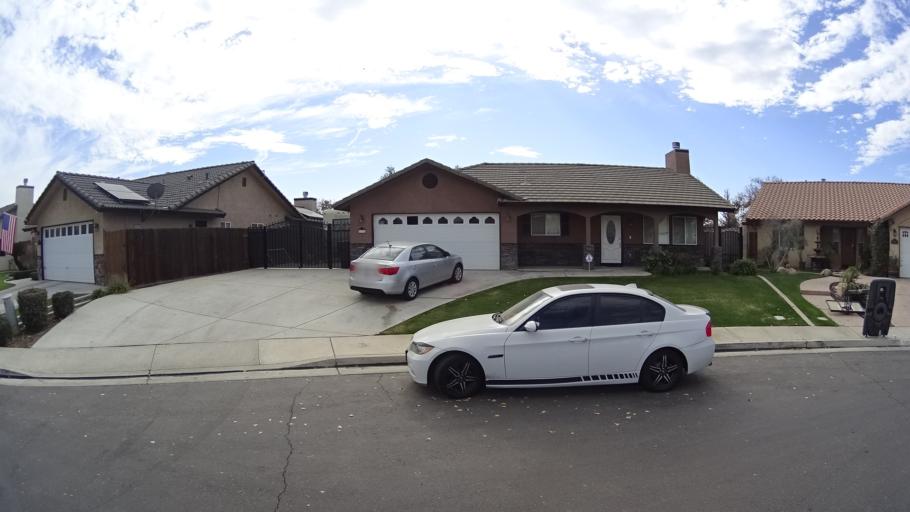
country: US
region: California
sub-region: Kern County
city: Rosedale
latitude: 35.3913
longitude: -119.1321
